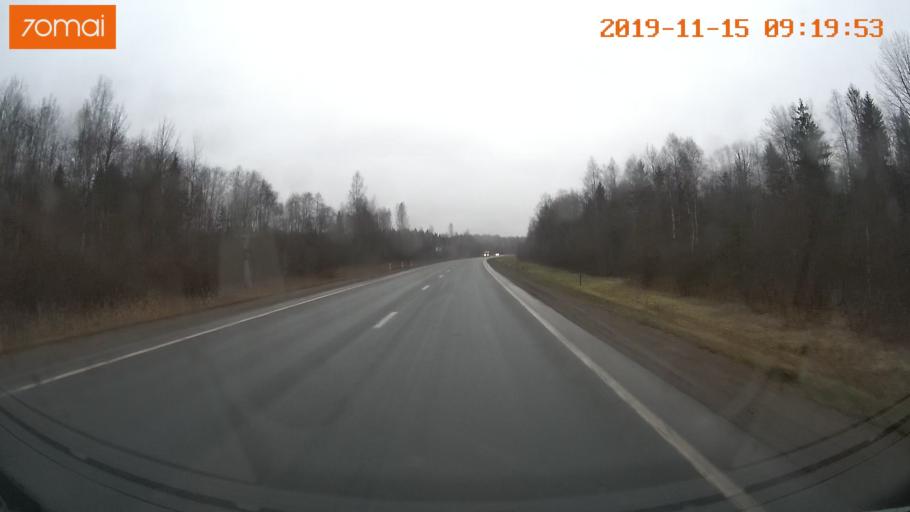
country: RU
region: Vologda
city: Tonshalovo
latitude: 59.2875
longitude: 38.0248
